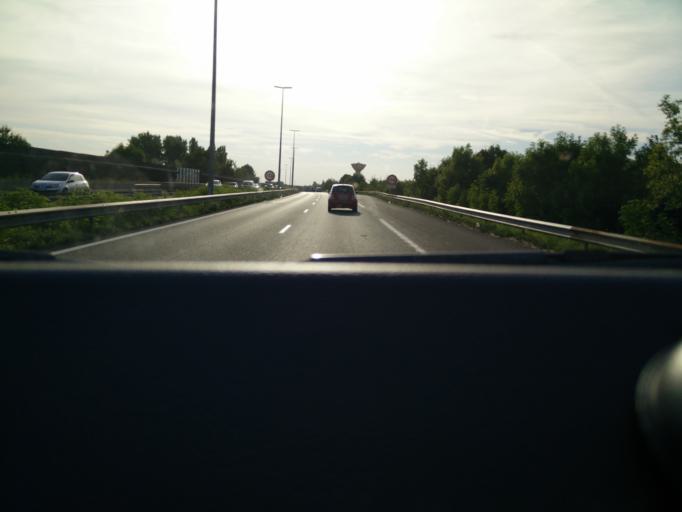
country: FR
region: Nord-Pas-de-Calais
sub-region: Departement du Pas-de-Calais
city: Montigny-en-Gohelle
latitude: 50.4324
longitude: 2.9474
